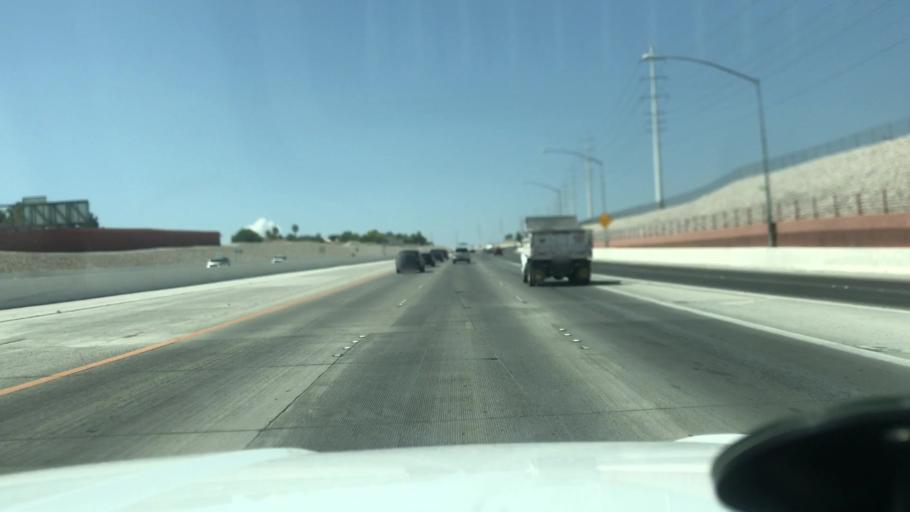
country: US
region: Nevada
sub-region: Clark County
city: Summerlin South
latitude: 36.2164
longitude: -115.3303
